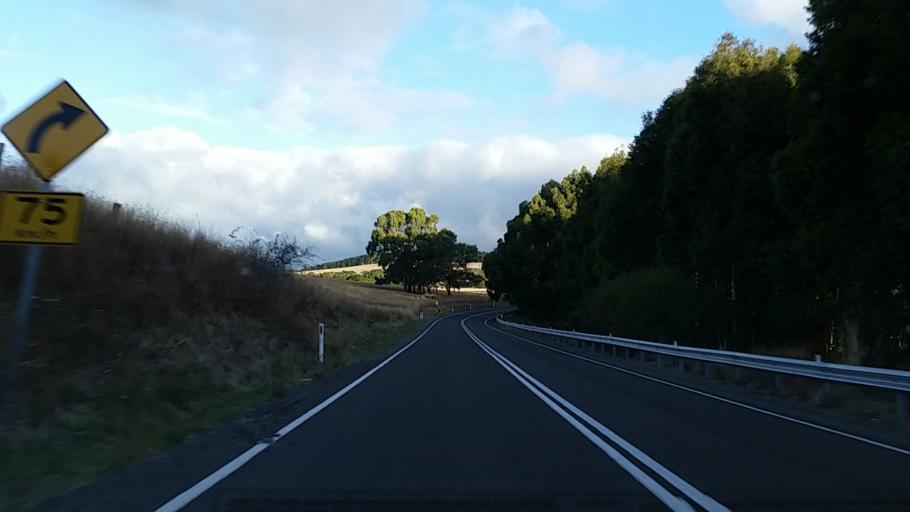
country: AU
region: South Australia
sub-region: Yankalilla
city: Normanville
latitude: -35.5604
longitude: 138.1997
